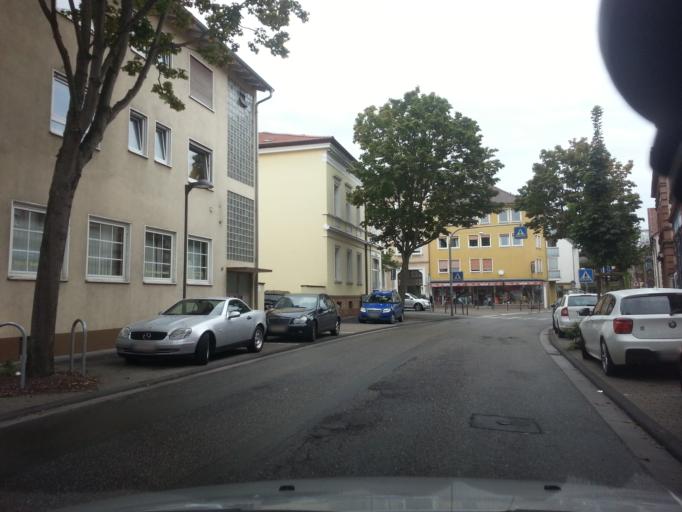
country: DE
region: Rheinland-Pfalz
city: Landau in der Pfalz
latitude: 49.1956
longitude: 8.1109
